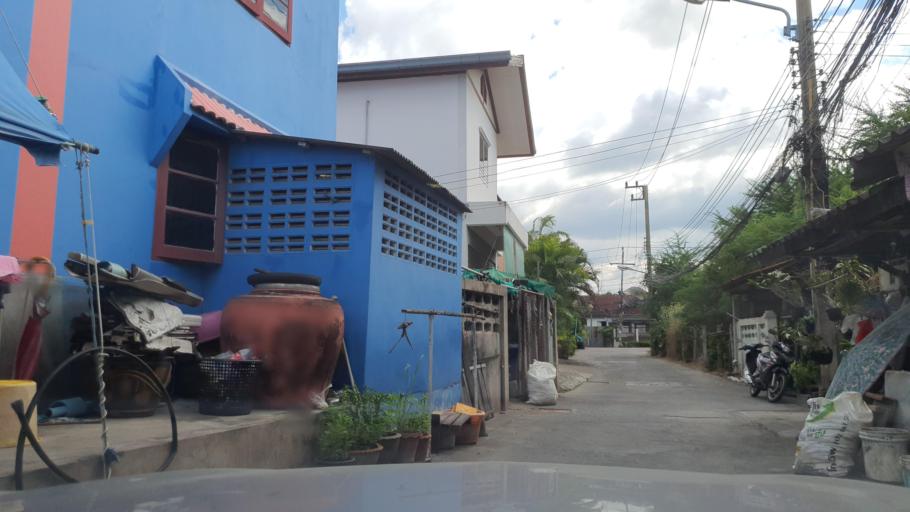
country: TH
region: Chon Buri
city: Chon Buri
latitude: 13.3698
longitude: 100.9833
